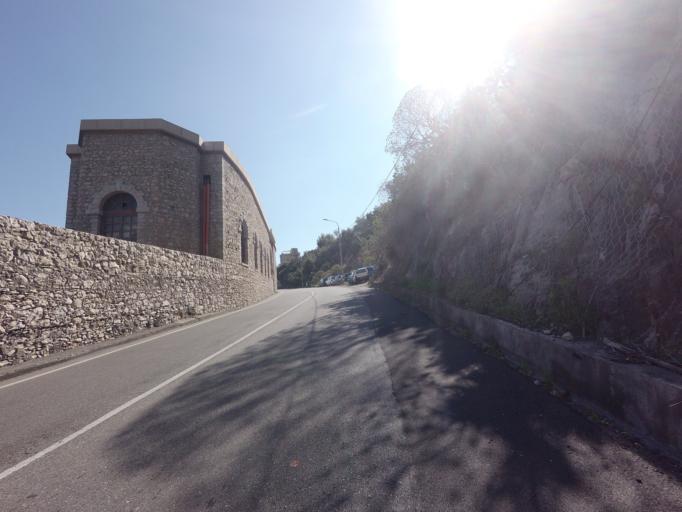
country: IT
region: Sicily
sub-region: Messina
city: Taormina
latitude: 37.8492
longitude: 15.2963
